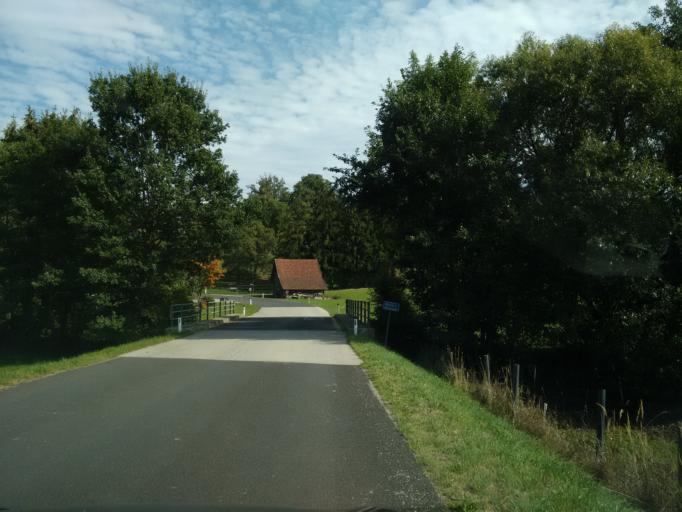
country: AT
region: Upper Austria
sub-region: Politischer Bezirk Kirchdorf an der Krems
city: Kremsmunster
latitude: 48.1183
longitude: 14.1346
